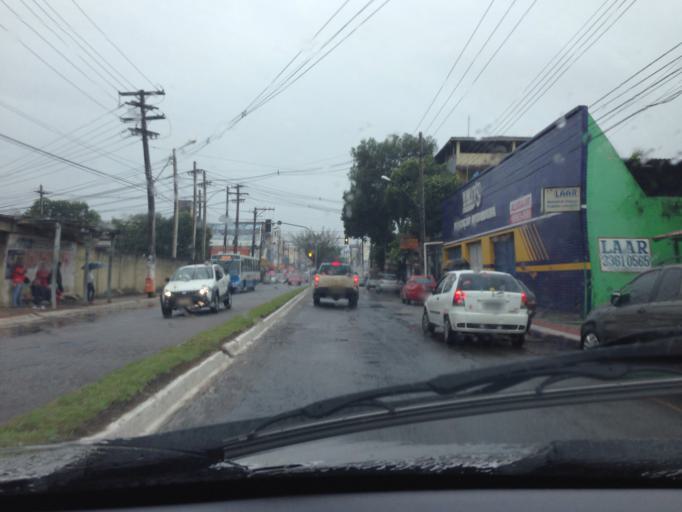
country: BR
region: Espirito Santo
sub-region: Guarapari
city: Guarapari
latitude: -20.6612
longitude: -40.5016
